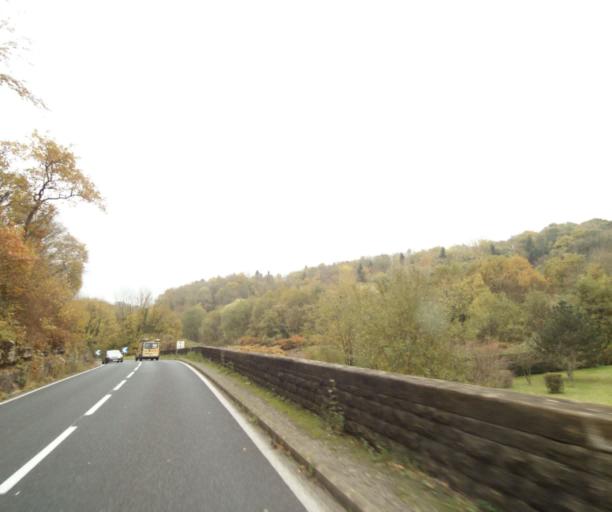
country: FR
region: Lorraine
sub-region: Departement de Meurthe-et-Moselle
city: Briey
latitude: 49.2410
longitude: 5.9465
